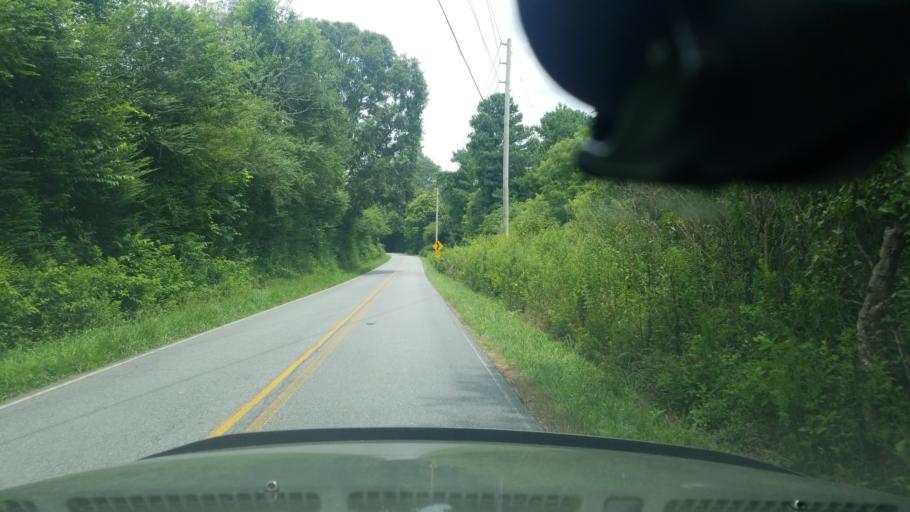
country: US
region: Georgia
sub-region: Forsyth County
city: Cumming
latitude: 34.2440
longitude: -84.2121
